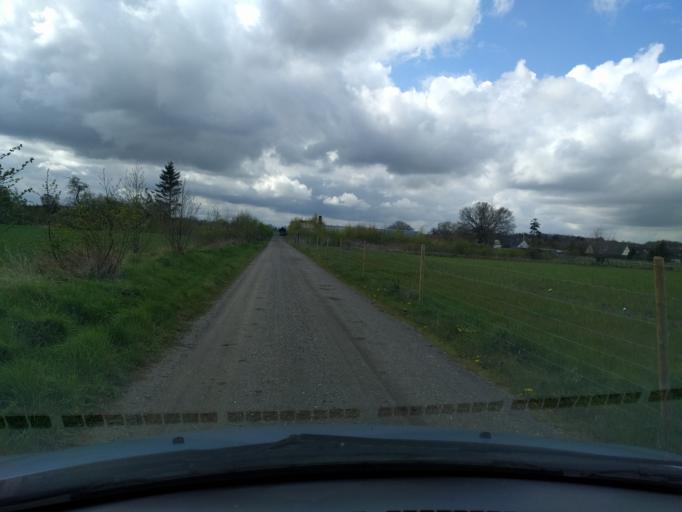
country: DK
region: South Denmark
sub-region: Odense Kommune
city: Bullerup
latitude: 55.4174
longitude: 10.4956
